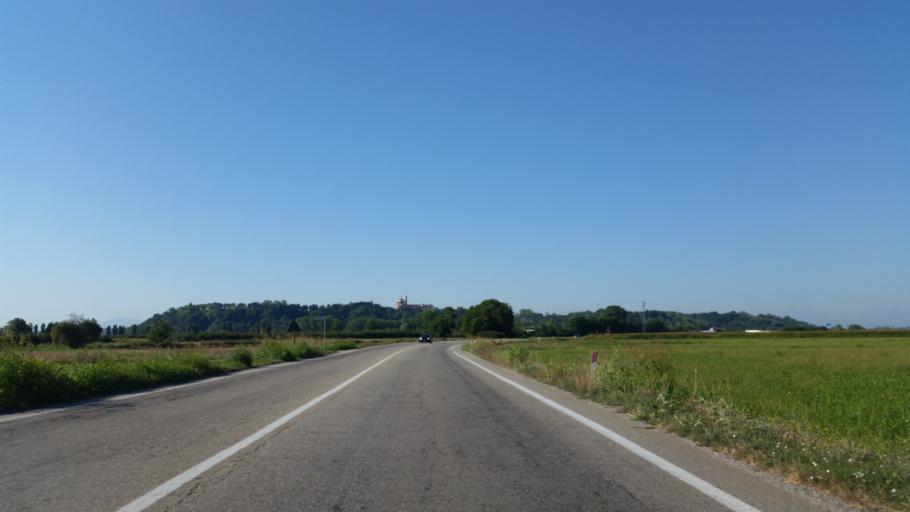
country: IT
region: Piedmont
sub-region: Provincia di Cuneo
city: Roreto
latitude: 44.6709
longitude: 7.8614
